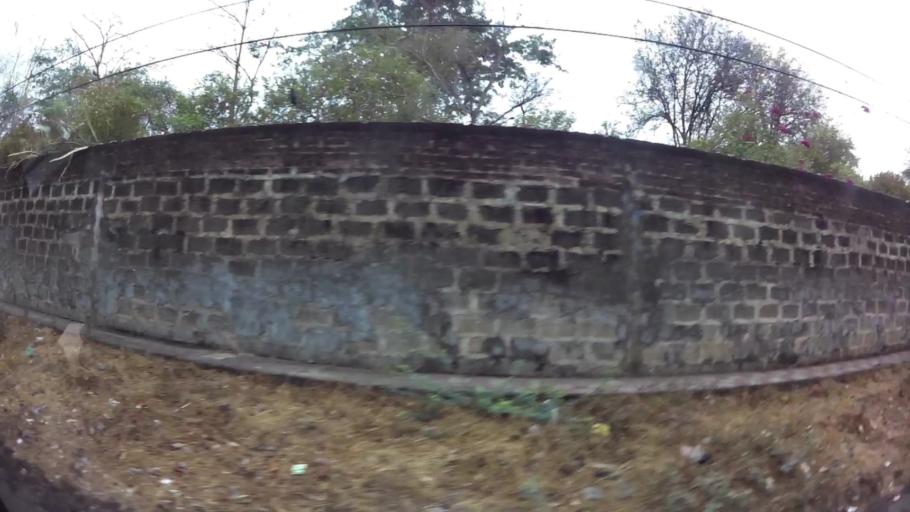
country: NI
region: Leon
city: Leon
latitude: 12.4486
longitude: -86.8770
